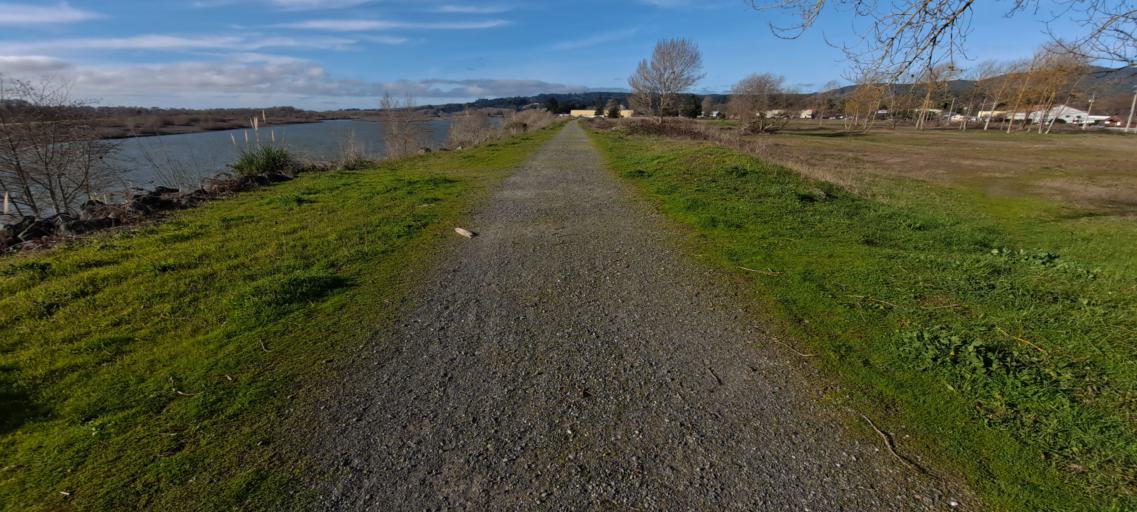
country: US
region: California
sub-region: Humboldt County
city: Fortuna
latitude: 40.5797
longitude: -124.1559
